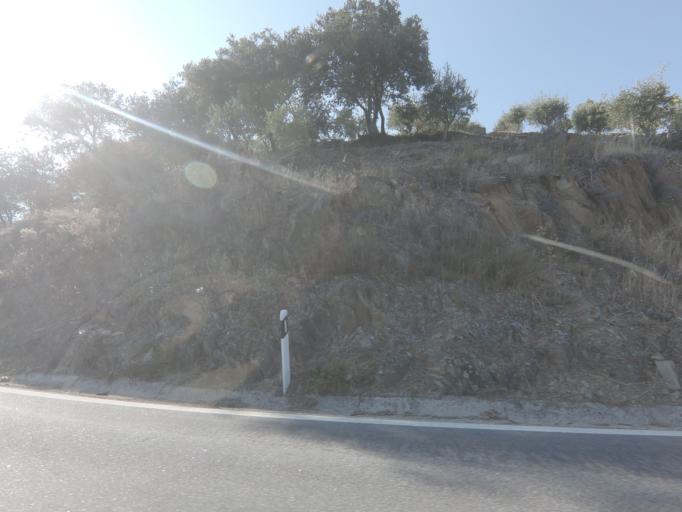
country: PT
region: Viseu
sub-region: Tabuaco
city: Tabuaco
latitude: 41.1347
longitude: -7.5680
